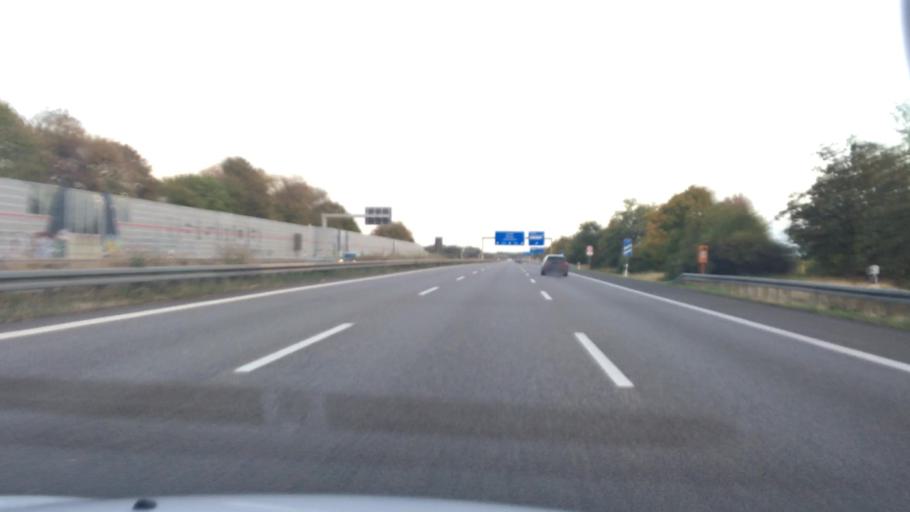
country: DE
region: Saxony
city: Rackwitz
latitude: 51.4005
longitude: 12.4098
